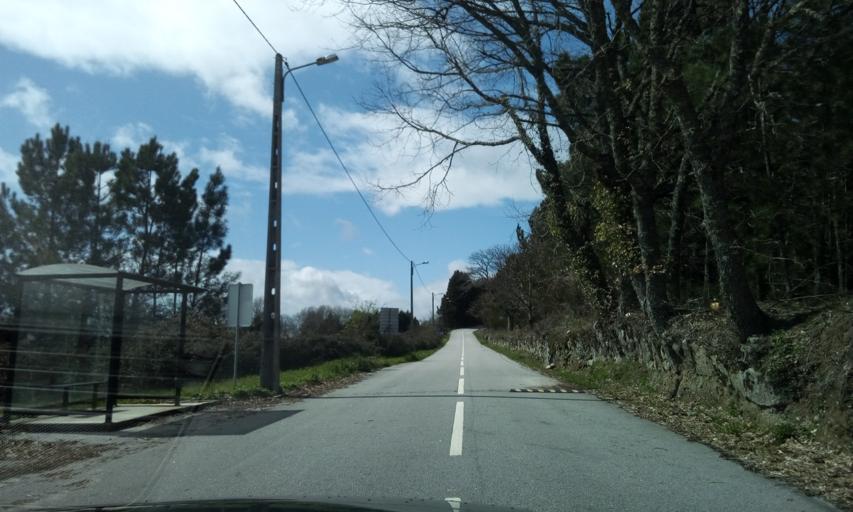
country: PT
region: Guarda
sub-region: Fornos de Algodres
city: Fornos de Algodres
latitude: 40.6312
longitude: -7.5418
